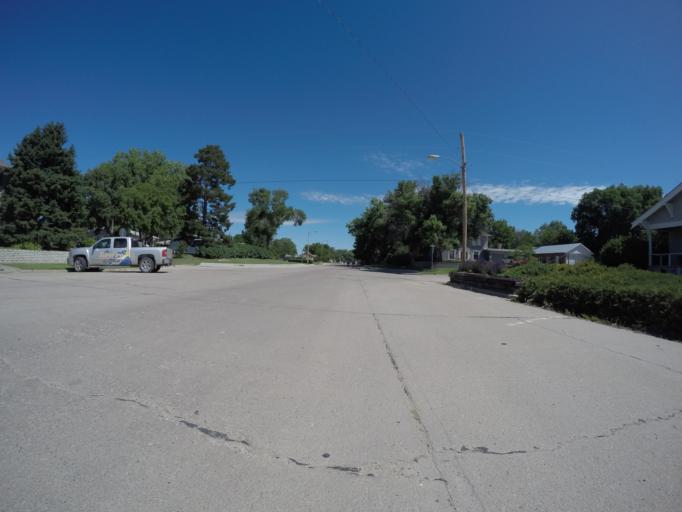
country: US
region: Kansas
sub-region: Rawlins County
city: Atwood
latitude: 39.8101
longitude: -101.0422
